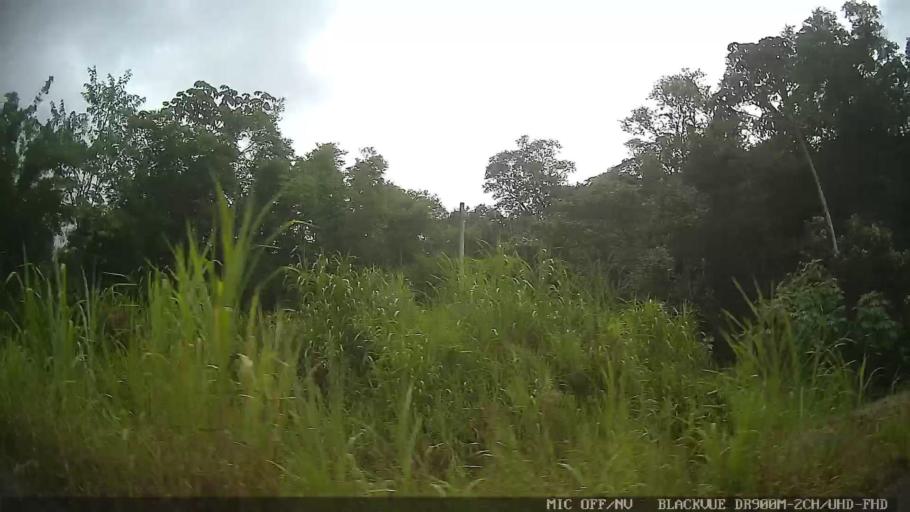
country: BR
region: Sao Paulo
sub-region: Aruja
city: Aruja
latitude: -23.4165
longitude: -46.2676
